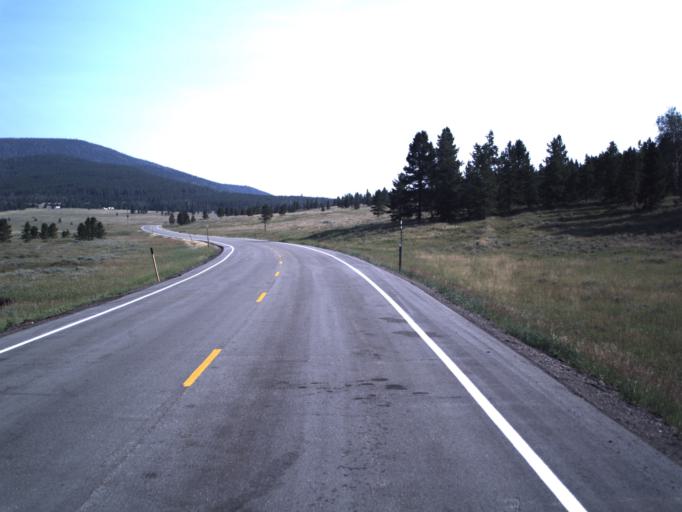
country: US
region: Utah
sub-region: Uintah County
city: Maeser
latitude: 40.7778
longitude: -109.4702
